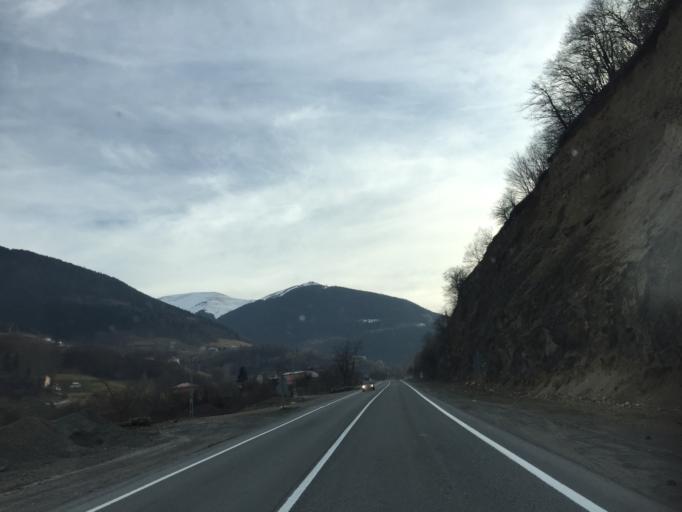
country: TR
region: Trabzon
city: Macka
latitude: 40.7223
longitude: 39.5190
